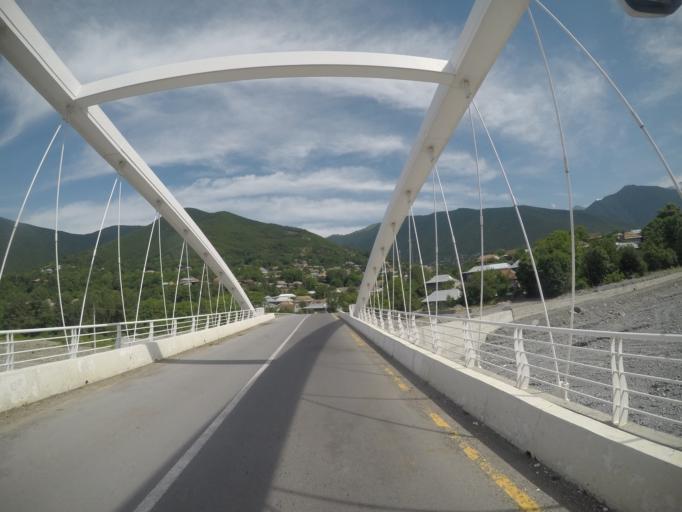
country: AZ
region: Shaki City
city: Sheki
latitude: 41.2455
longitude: 47.1888
